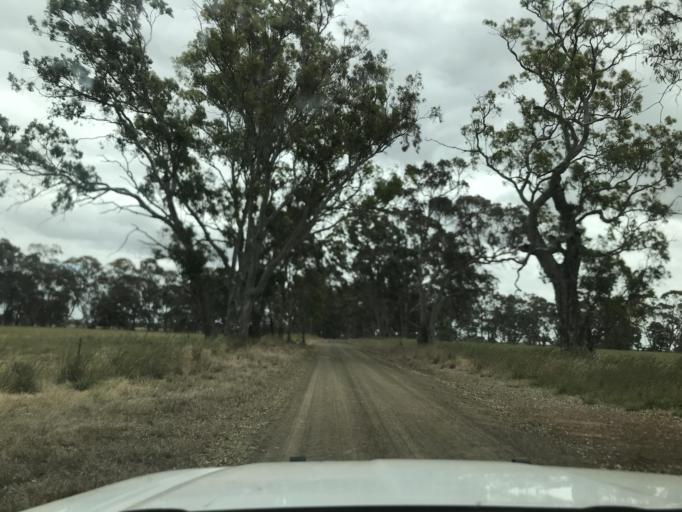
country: AU
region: South Australia
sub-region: Naracoorte and Lucindale
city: Naracoorte
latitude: -36.9471
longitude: 141.3102
